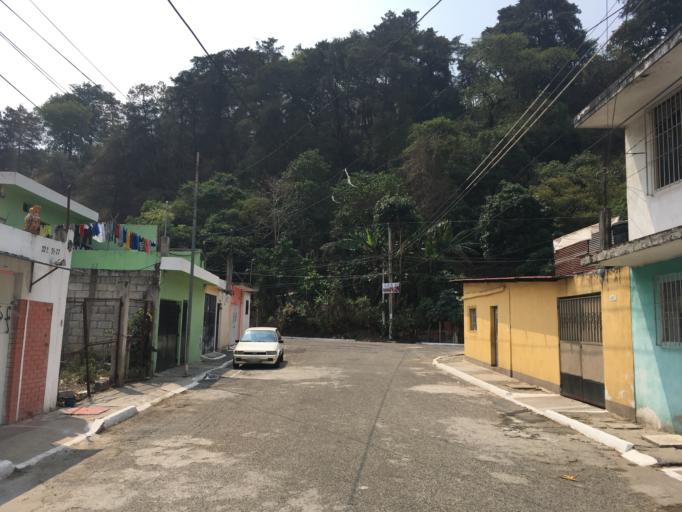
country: GT
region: Guatemala
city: Petapa
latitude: 14.5175
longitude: -90.5407
